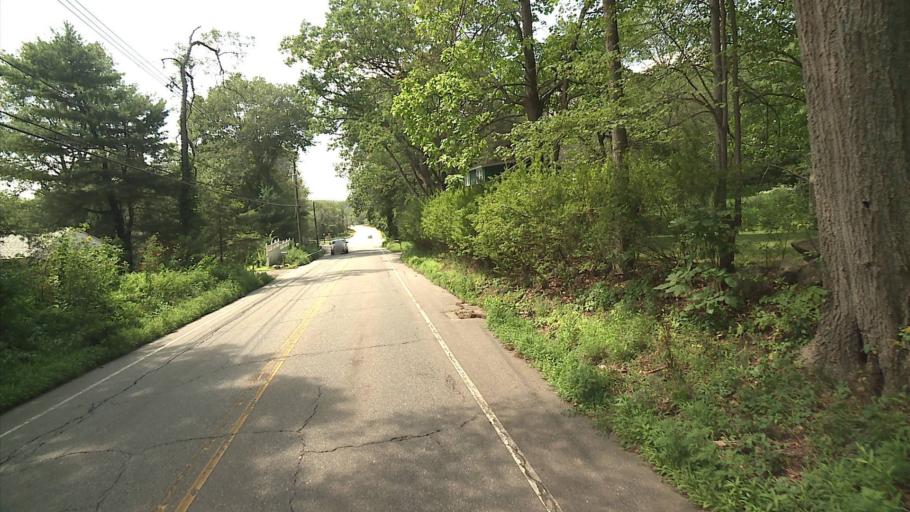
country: US
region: Connecticut
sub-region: New London County
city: Colchester
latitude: 41.5820
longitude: -72.3555
